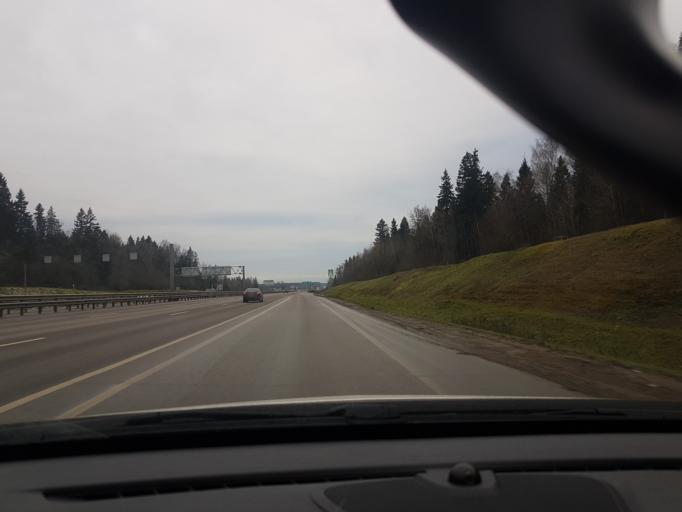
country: RU
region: Moskovskaya
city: Kostrovo
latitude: 55.8541
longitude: 36.7773
